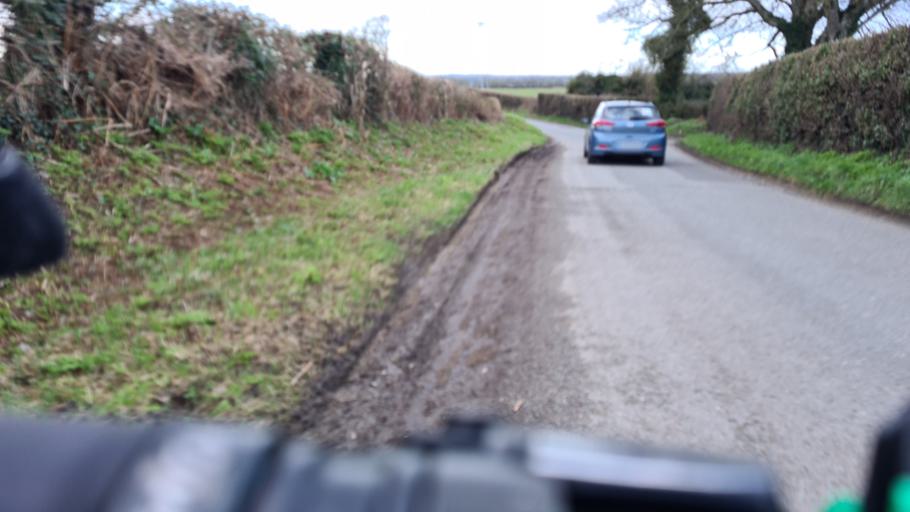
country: IE
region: Leinster
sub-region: Kildare
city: Maynooth
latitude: 53.3488
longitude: -6.5947
